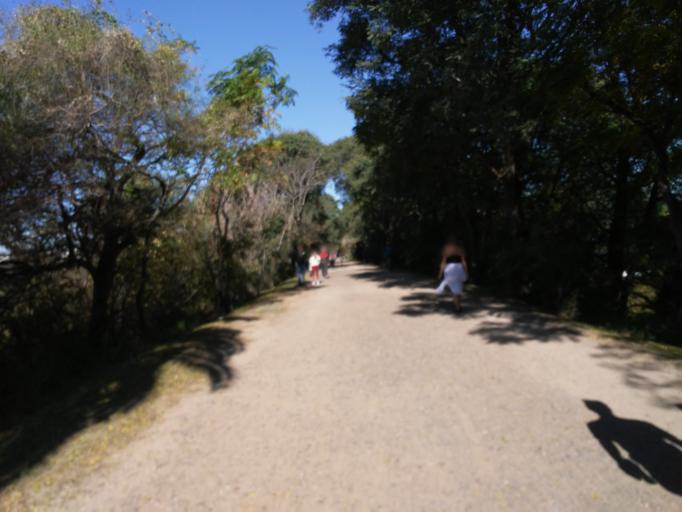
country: AR
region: Buenos Aires F.D.
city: Buenos Aires
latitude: -34.6143
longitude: -58.3557
